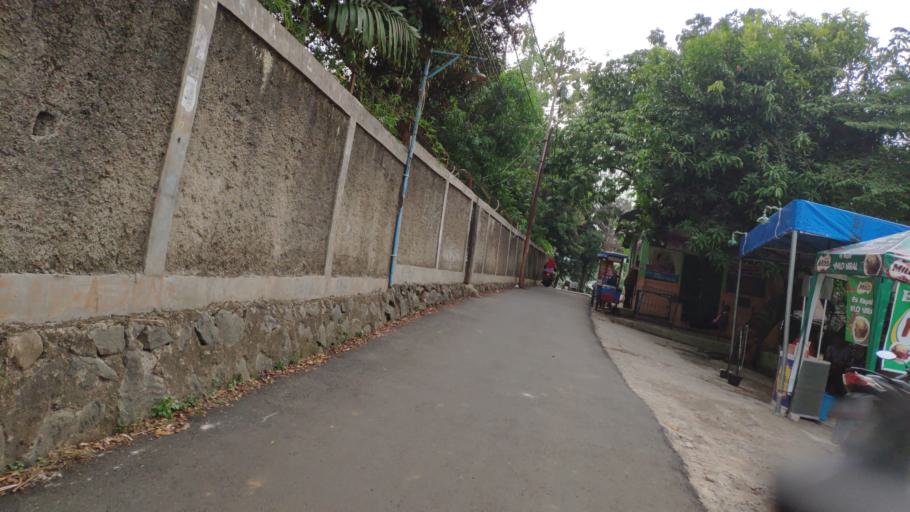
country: ID
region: West Java
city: Depok
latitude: -6.3368
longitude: 106.8328
